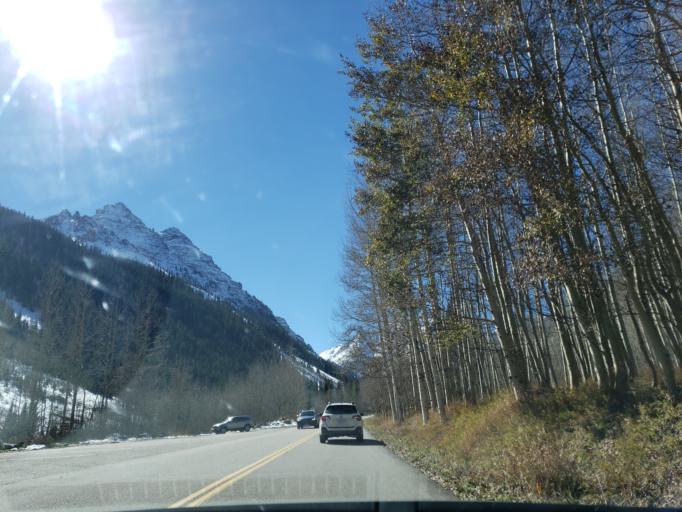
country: US
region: Colorado
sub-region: Pitkin County
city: Snowmass Village
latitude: 39.1019
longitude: -106.9348
